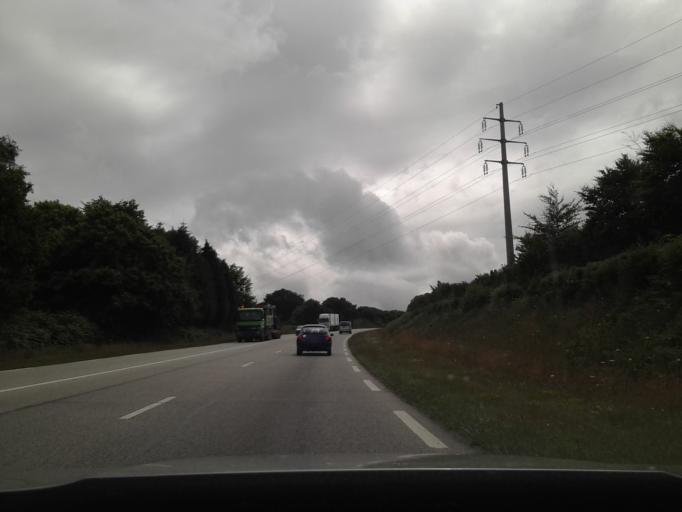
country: FR
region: Lower Normandy
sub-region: Departement de la Manche
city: La Glacerie
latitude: 49.6096
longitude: -1.5866
